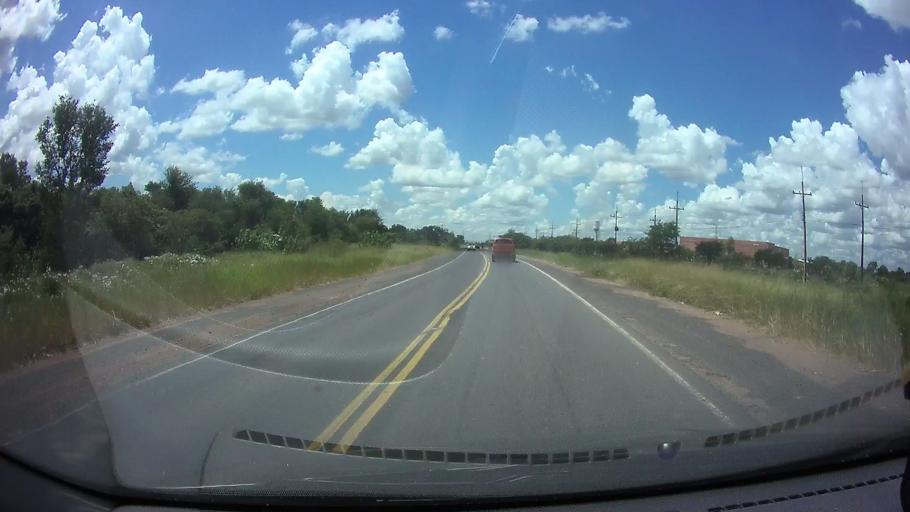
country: PY
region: Central
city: Colonia Mariano Roque Alonso
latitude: -25.1859
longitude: -57.5941
